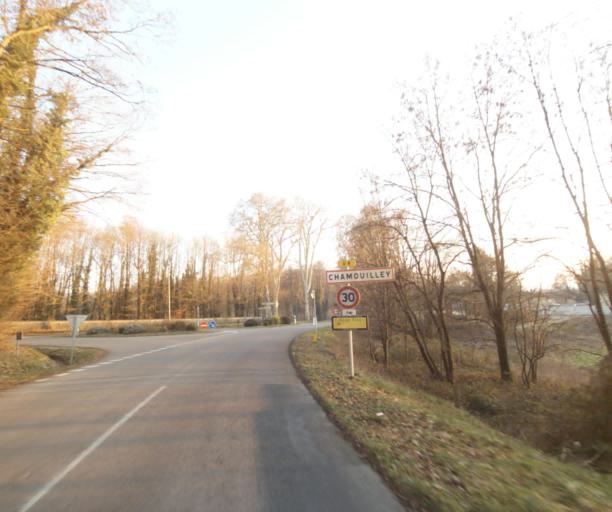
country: FR
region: Lorraine
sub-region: Departement de la Meuse
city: Ancerville
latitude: 48.6116
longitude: 5.0464
